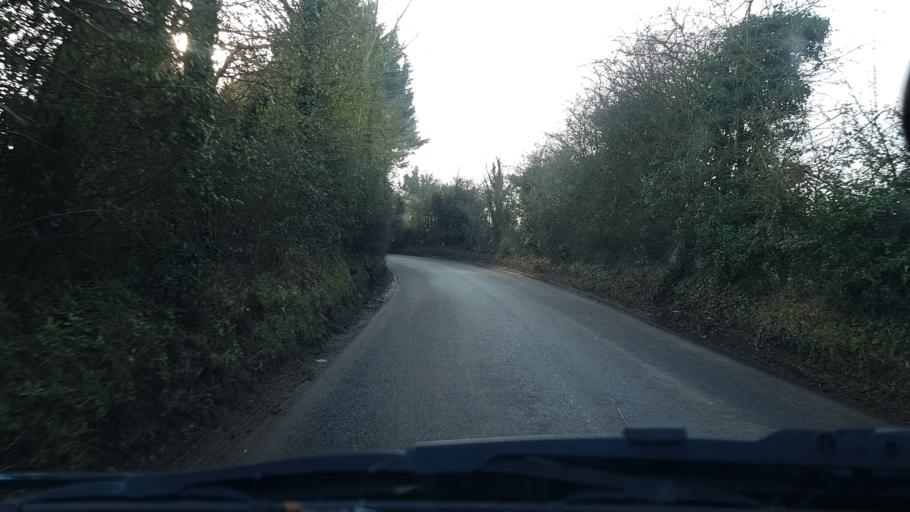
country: GB
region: England
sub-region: Wiltshire
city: Pewsey
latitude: 51.3448
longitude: -1.7538
